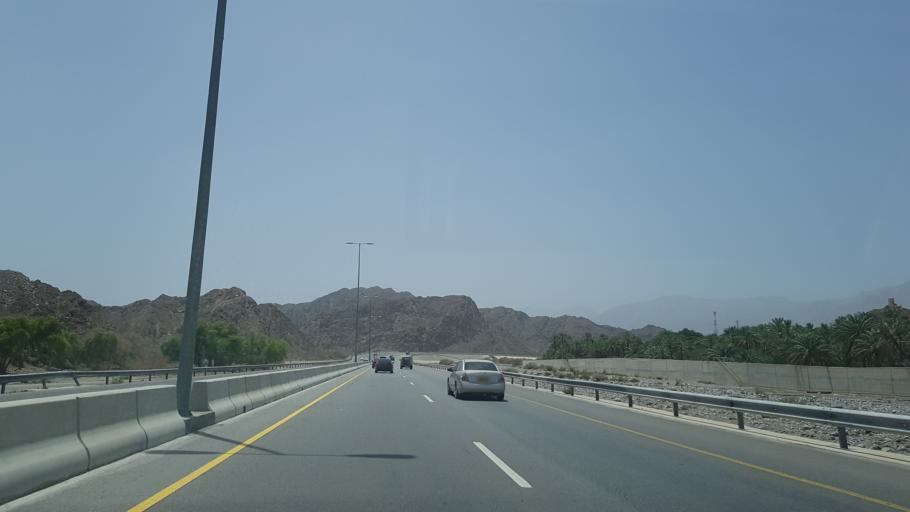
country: OM
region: Muhafazat ad Dakhiliyah
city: Sufalat Sama'il
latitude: 23.3498
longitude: 58.0189
